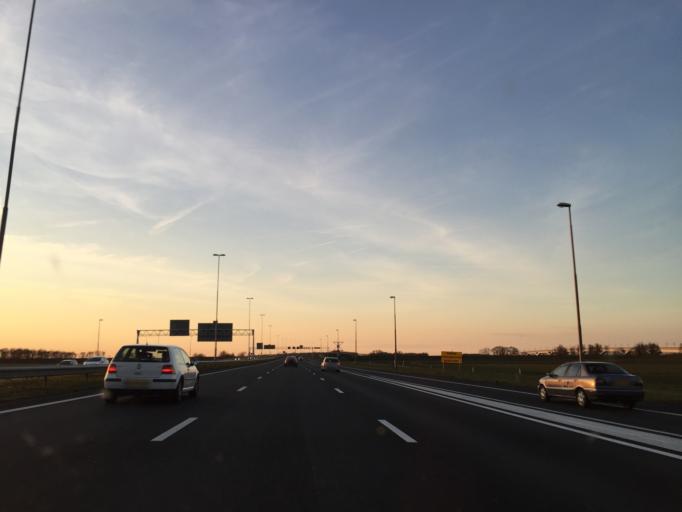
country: NL
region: South Holland
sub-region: Gemeente Strijen
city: Strijen
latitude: 51.7054
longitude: 4.6455
